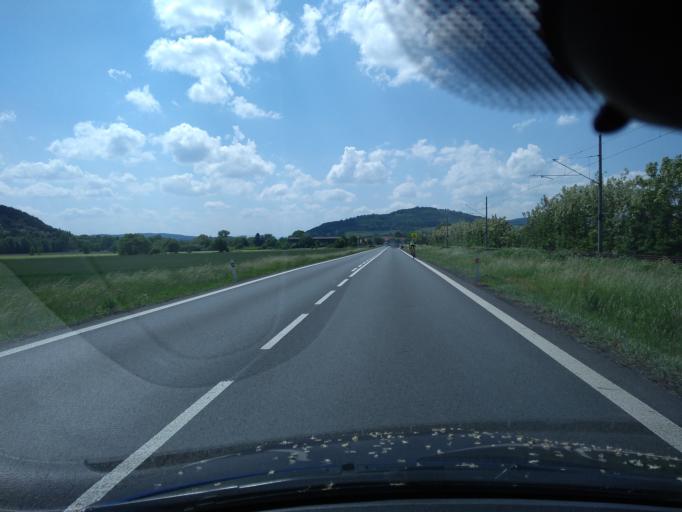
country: CZ
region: Plzensky
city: Prestice
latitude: 49.5326
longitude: 13.3044
